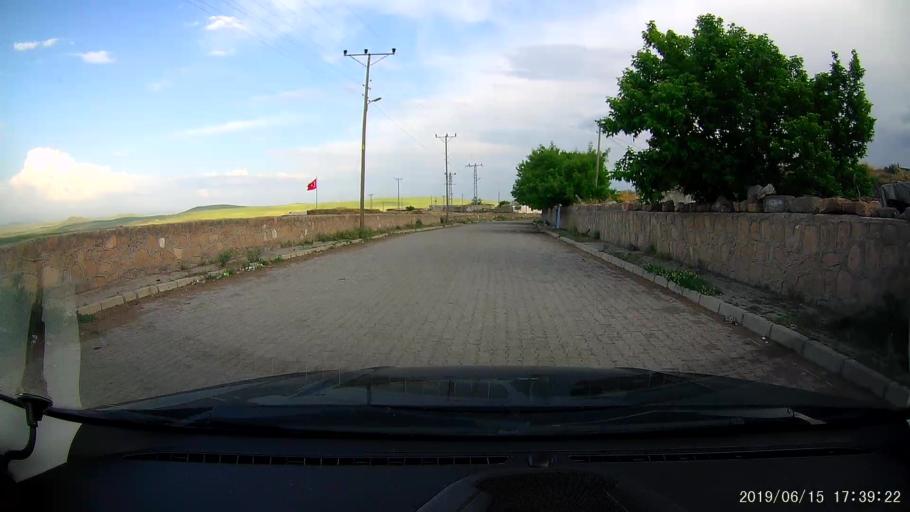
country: TR
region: Kars
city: Basgedikler
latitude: 40.5164
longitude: 43.5700
